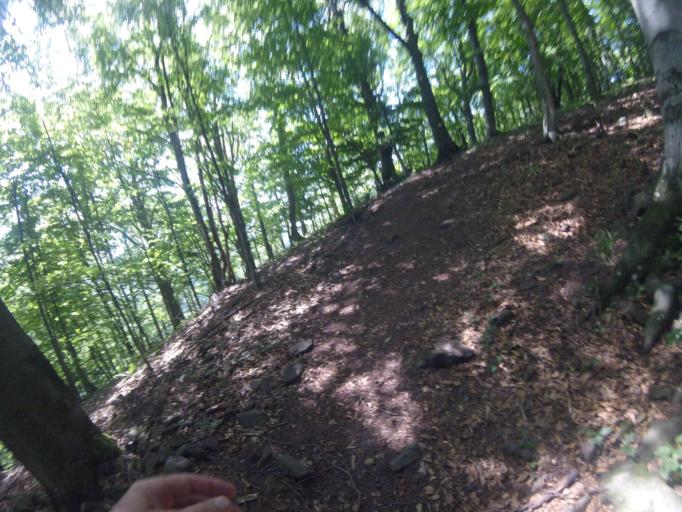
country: SK
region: Nitriansky
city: Sahy
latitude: 47.9721
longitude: 18.8844
